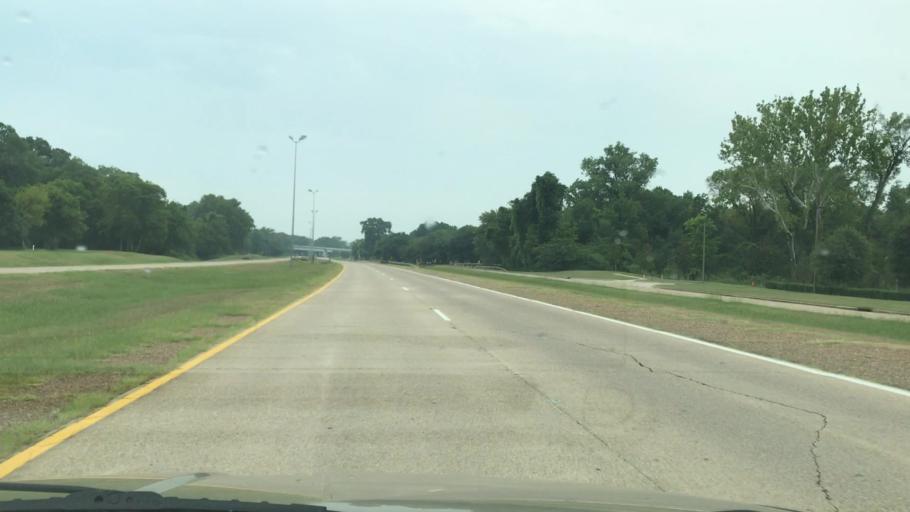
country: US
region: Louisiana
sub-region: Bossier Parish
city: Bossier City
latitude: 32.4963
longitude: -93.7102
